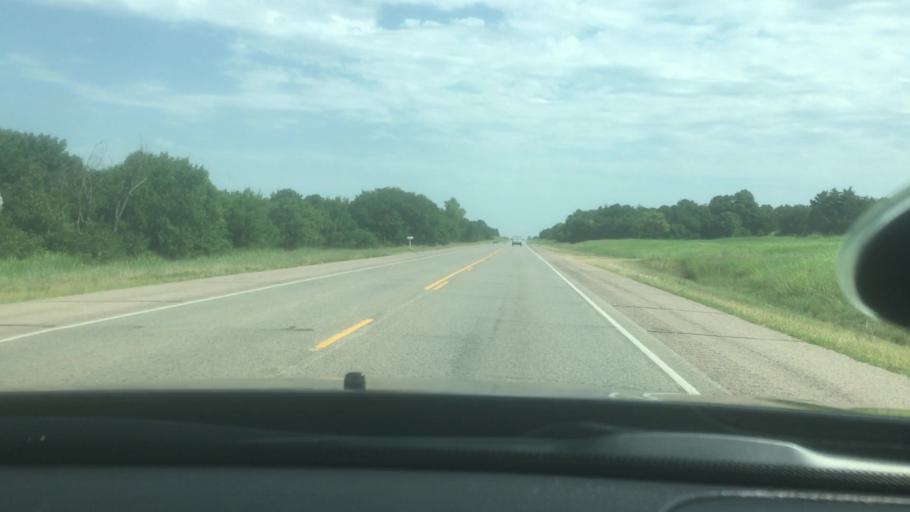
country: US
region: Oklahoma
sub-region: Seminole County
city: Konawa
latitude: 35.0094
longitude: -96.9318
